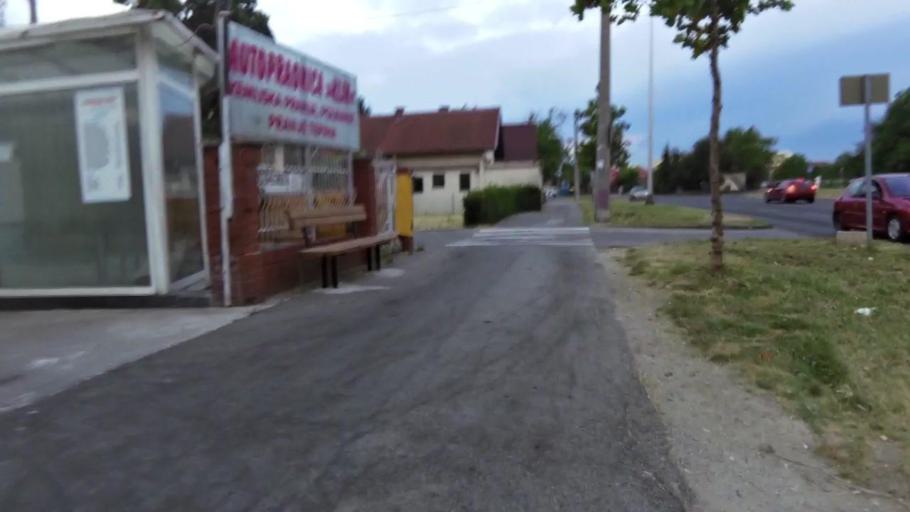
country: HR
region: Grad Zagreb
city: Dubrava
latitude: 45.8316
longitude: 16.0639
